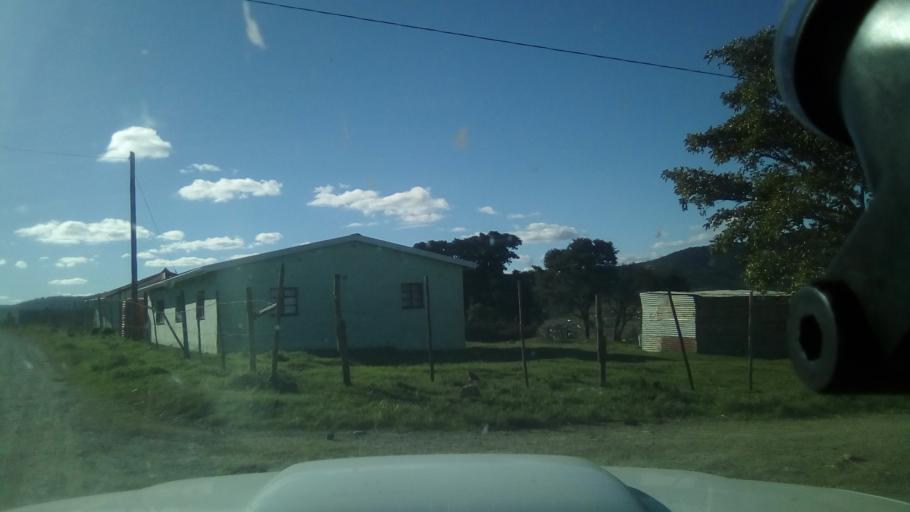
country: ZA
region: Eastern Cape
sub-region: Buffalo City Metropolitan Municipality
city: Bhisho
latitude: -32.7444
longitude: 27.3516
